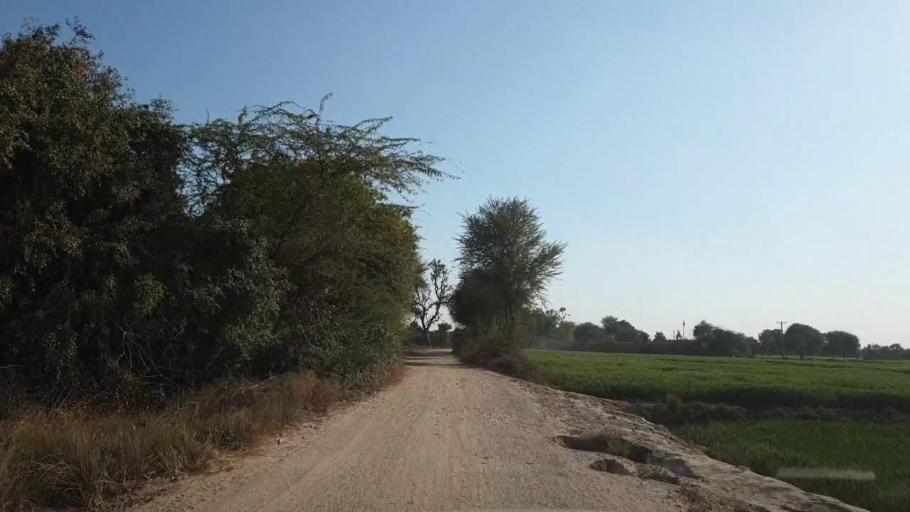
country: PK
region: Sindh
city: Tando Adam
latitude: 25.6925
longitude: 68.6855
